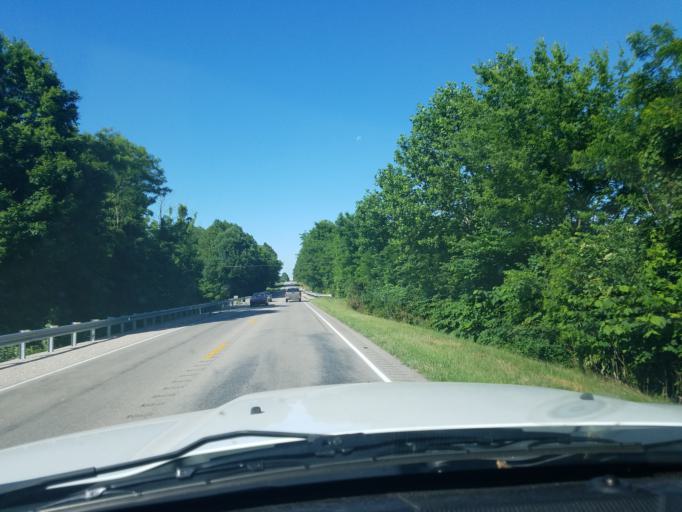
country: US
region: Kentucky
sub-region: Barren County
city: Glasgow
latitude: 36.9495
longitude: -85.9683
